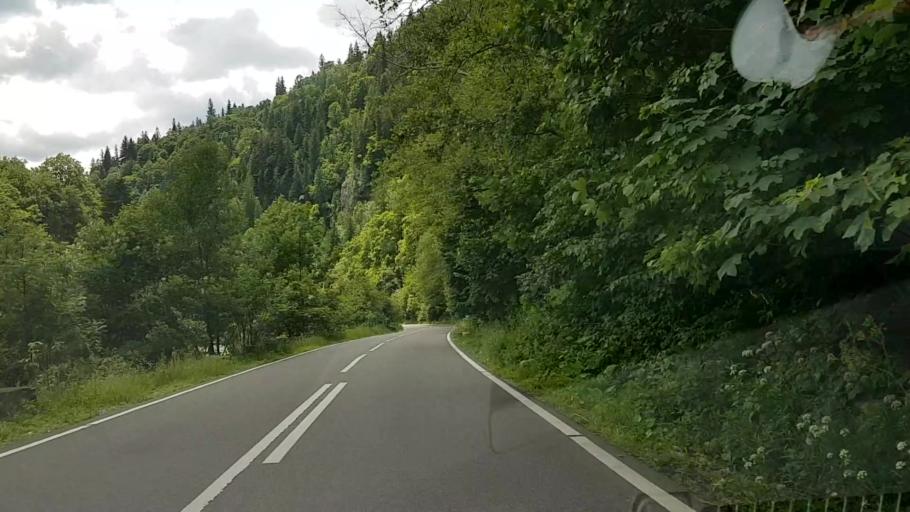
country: RO
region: Suceava
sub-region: Comuna Crucea
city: Crucea
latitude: 47.3177
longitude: 25.6260
